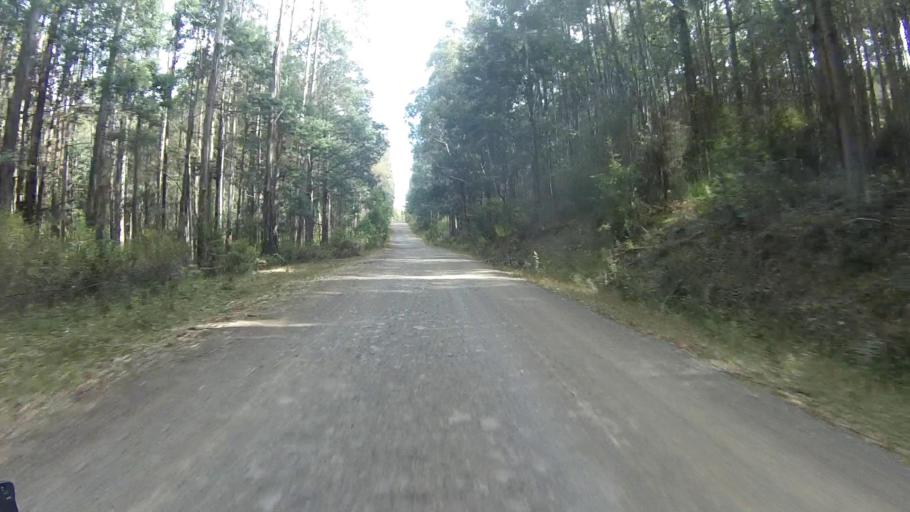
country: AU
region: Tasmania
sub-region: Sorell
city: Sorell
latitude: -42.7467
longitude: 147.8290
